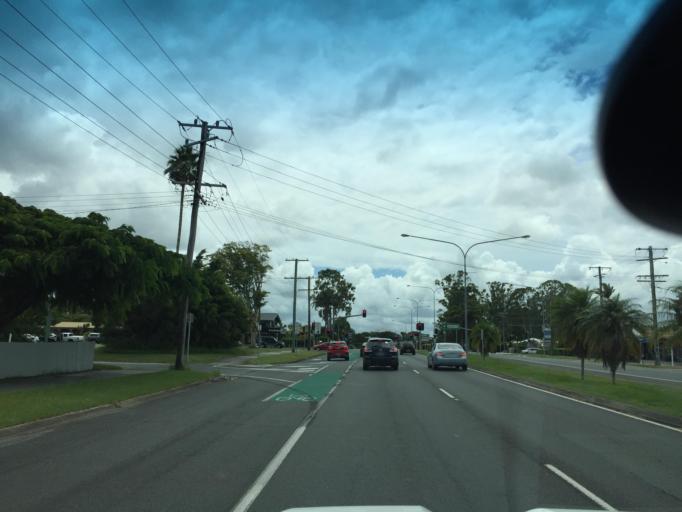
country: AU
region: Queensland
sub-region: Moreton Bay
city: Caboolture South
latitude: -27.0932
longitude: 152.9497
